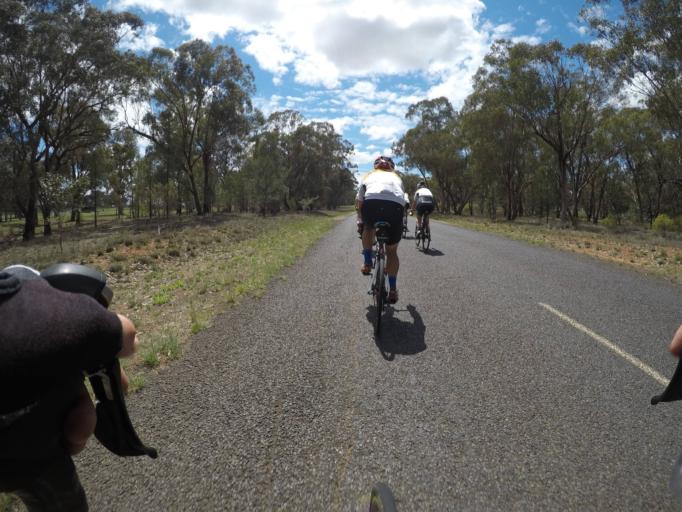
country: AU
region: New South Wales
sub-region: Dubbo Municipality
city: Dubbo
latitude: -32.3832
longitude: 148.5745
